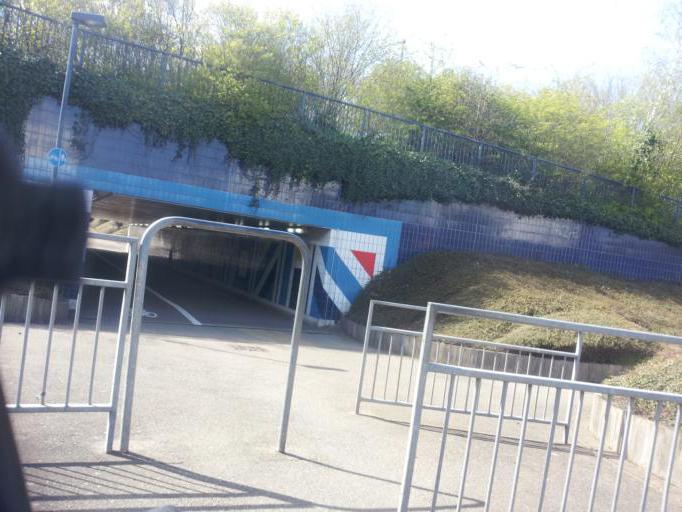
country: GB
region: England
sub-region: Kent
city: Gillingham
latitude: 51.3711
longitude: 0.5697
